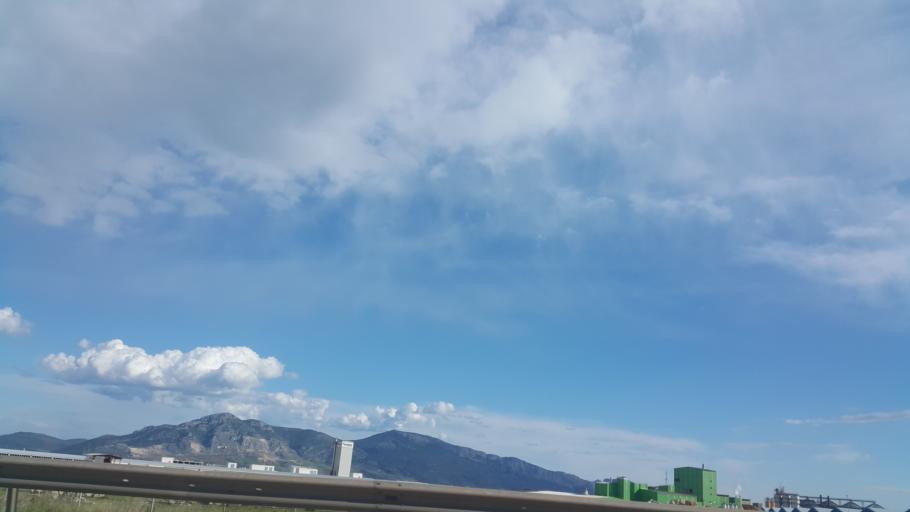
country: TR
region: Adana
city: Yakapinar
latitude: 36.9912
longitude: 35.6198
